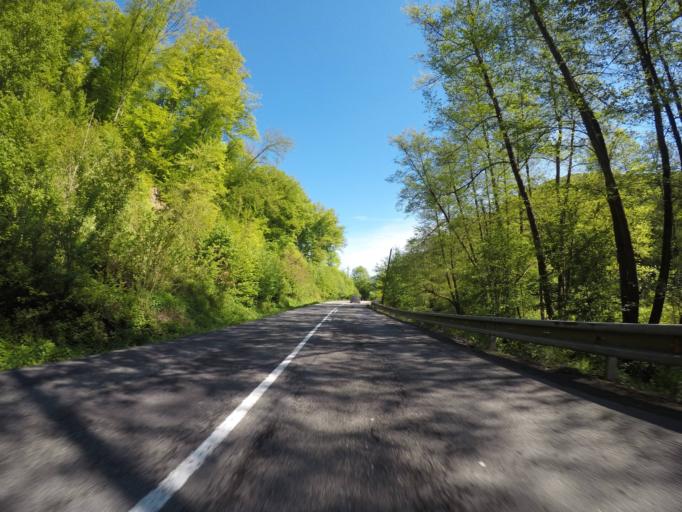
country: SK
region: Banskobystricky
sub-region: Okres Banska Bystrica
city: Banska Stiavnica
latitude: 48.5194
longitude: 19.0044
